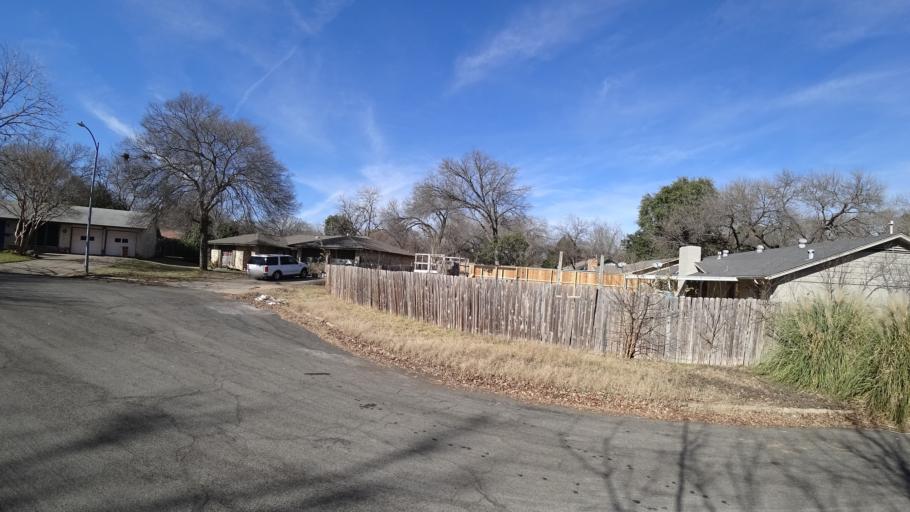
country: US
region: Texas
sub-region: Travis County
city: Wells Branch
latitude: 30.3736
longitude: -97.7056
